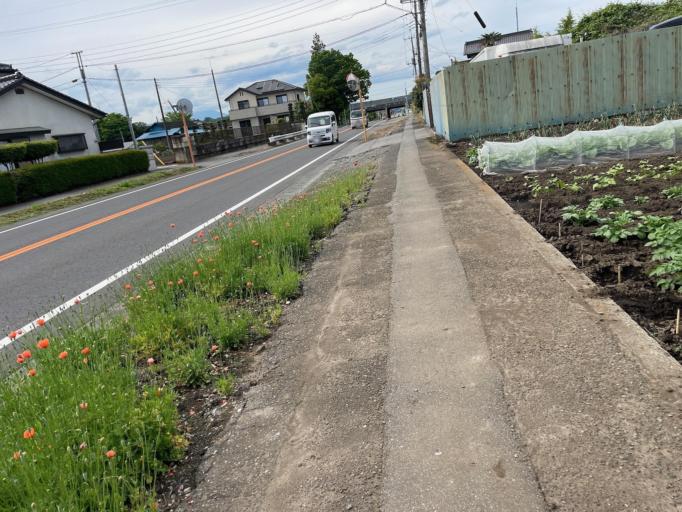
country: JP
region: Tochigi
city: Kanuma
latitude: 36.4951
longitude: 139.7546
